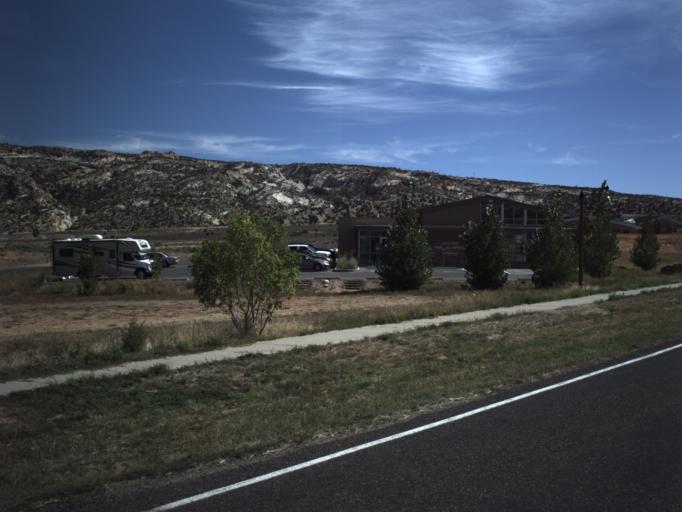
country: US
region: Utah
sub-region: Wayne County
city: Loa
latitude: 37.7669
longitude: -111.5914
